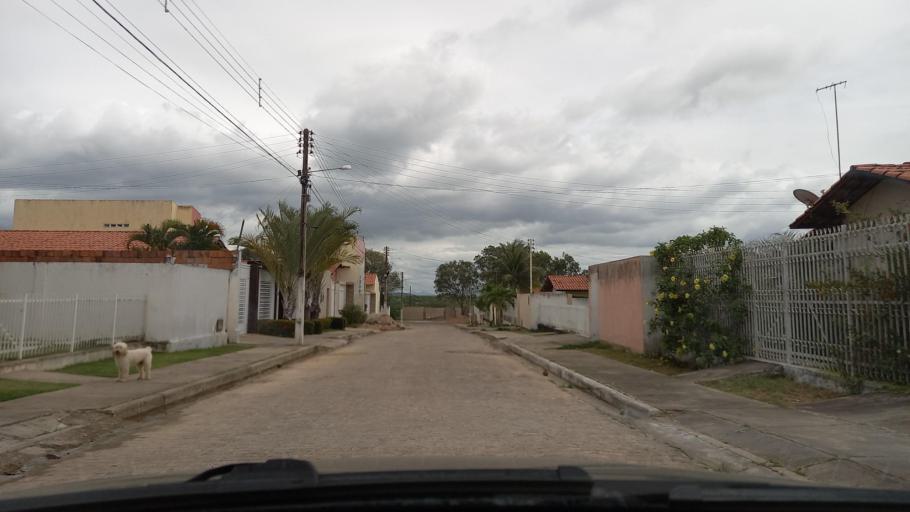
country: BR
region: Sergipe
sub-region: Caninde De Sao Francisco
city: Caninde de Sao Francisco
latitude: -9.6152
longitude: -37.7661
